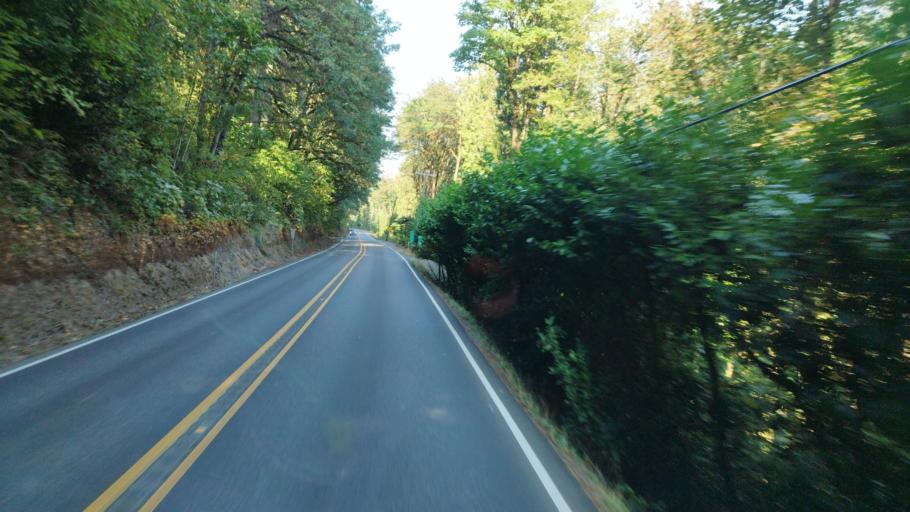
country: US
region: Oregon
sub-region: Washington County
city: Bethany
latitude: 45.6387
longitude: -122.8614
